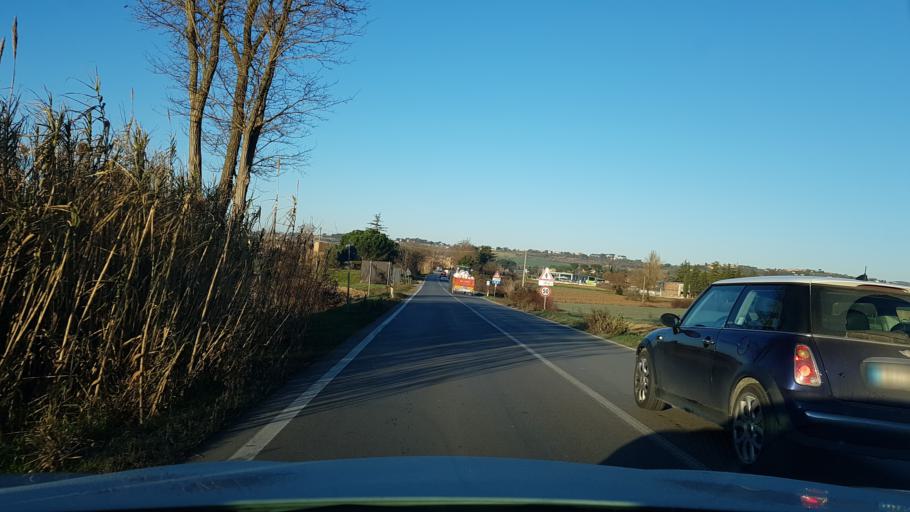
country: IT
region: Umbria
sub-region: Provincia di Perugia
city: San Martino in Campo
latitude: 43.0357
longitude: 12.4205
